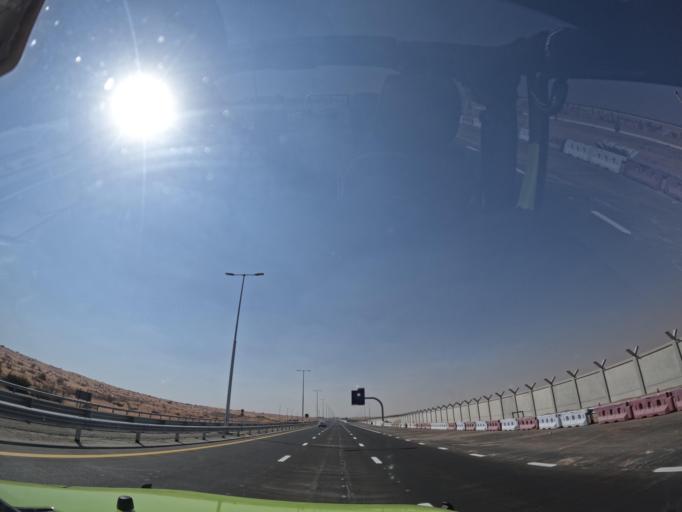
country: OM
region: Al Buraimi
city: Al Buraymi
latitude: 24.7697
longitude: 55.8101
